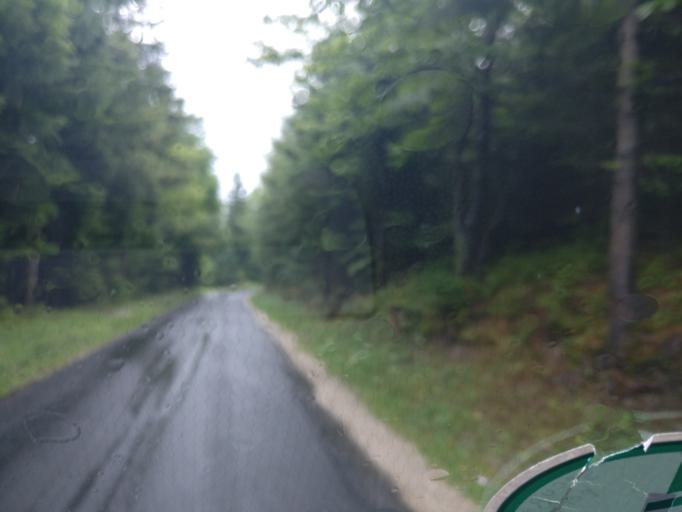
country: AT
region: Lower Austria
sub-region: Politischer Bezirk Neunkirchen
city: Gloggnitz
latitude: 47.6715
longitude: 15.9093
